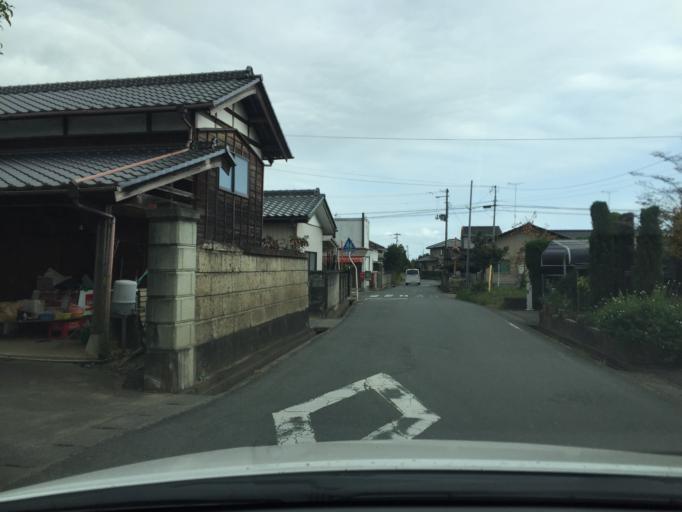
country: JP
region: Ibaraki
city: Kitaibaraki
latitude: 36.8978
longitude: 140.7637
